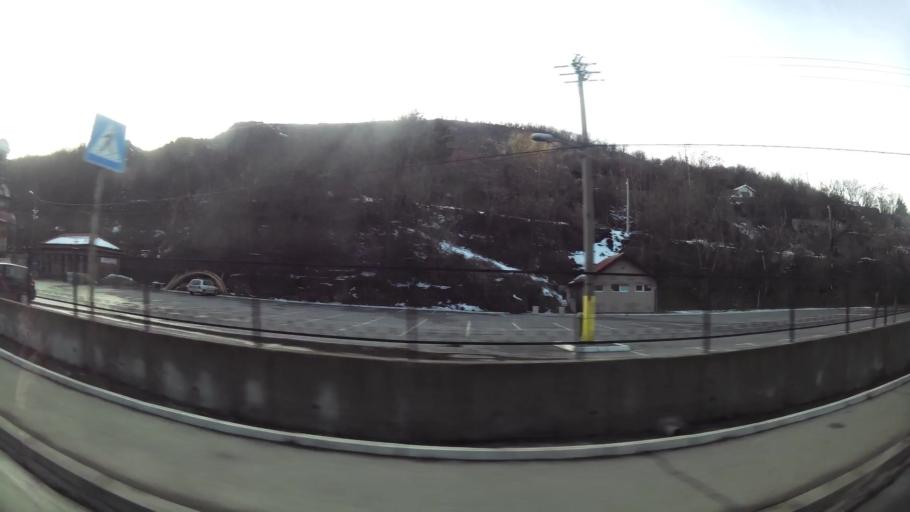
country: RS
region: Central Serbia
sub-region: Belgrade
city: Rakovica
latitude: 44.7319
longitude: 20.4470
